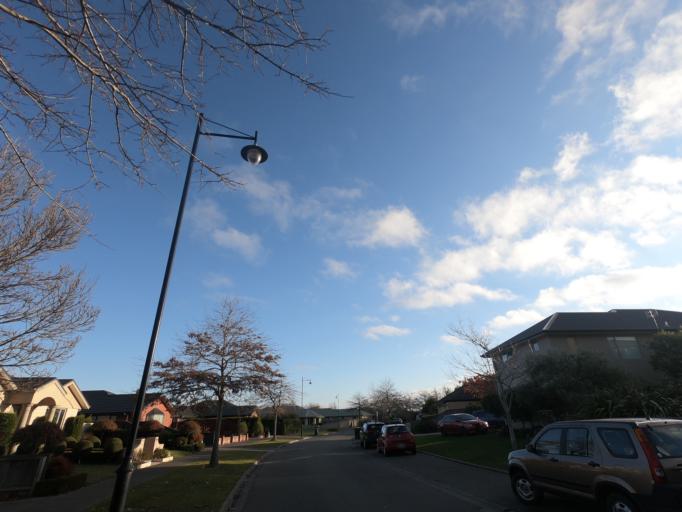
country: NZ
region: Canterbury
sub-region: Selwyn District
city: Prebbleton
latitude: -43.5662
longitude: 172.5708
